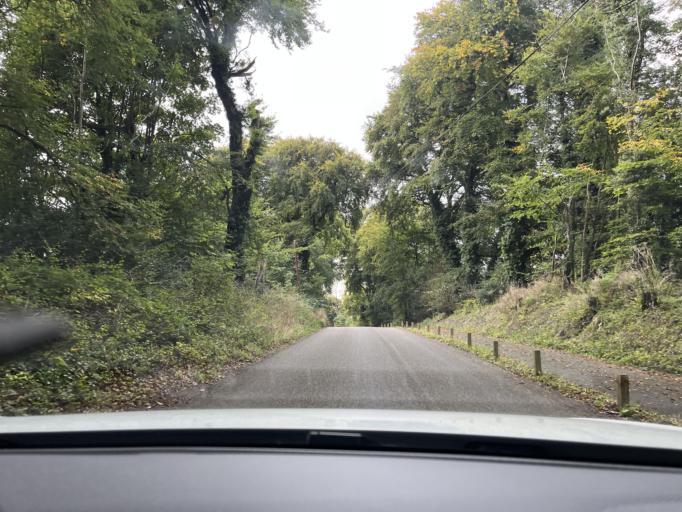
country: IE
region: Connaught
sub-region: Roscommon
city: Boyle
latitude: 53.9771
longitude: -8.2712
